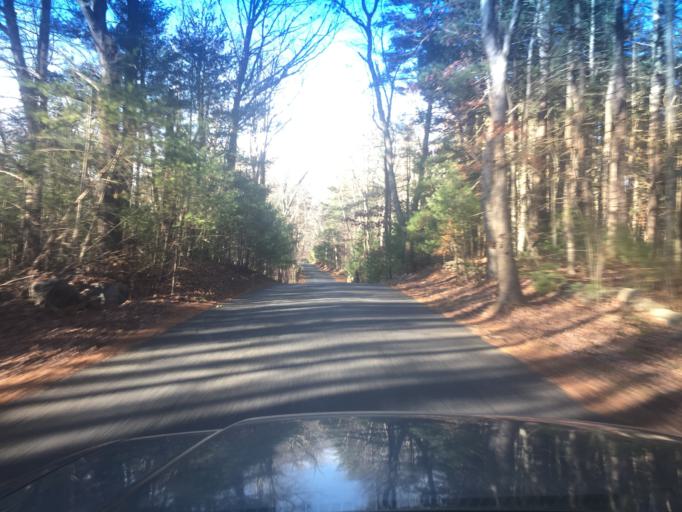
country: US
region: Massachusetts
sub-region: Middlesex County
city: Holliston
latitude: 42.2162
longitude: -71.4646
